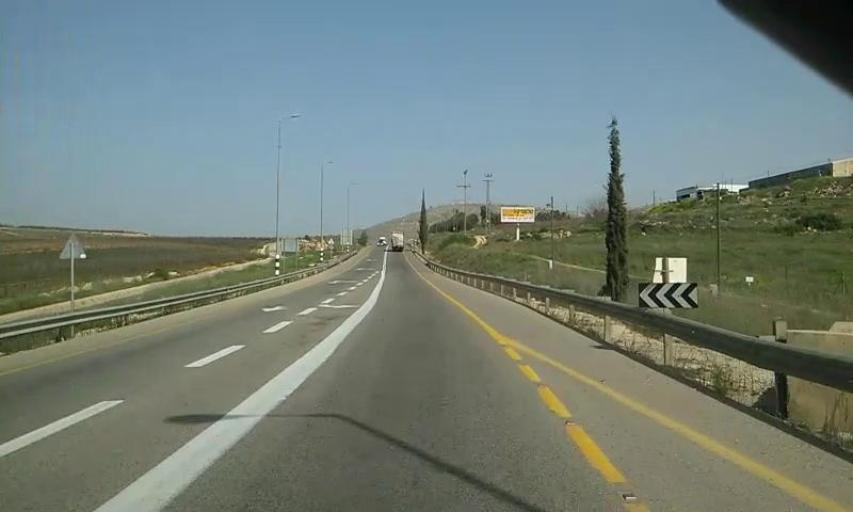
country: PS
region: West Bank
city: Qaryut
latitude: 32.0543
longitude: 35.2873
